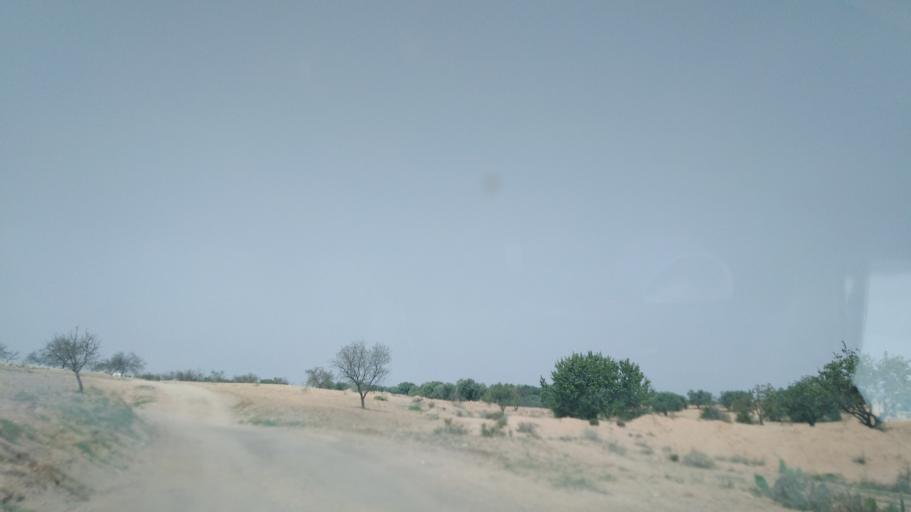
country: TN
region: Safaqis
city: Sfax
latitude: 34.6390
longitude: 10.5673
